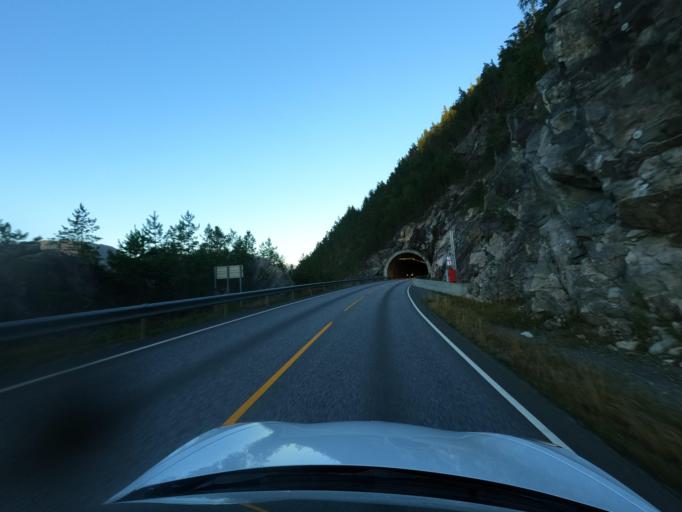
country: NO
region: Sogn og Fjordane
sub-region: Laerdal
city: Laerdalsoyri
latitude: 61.1757
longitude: 7.4609
